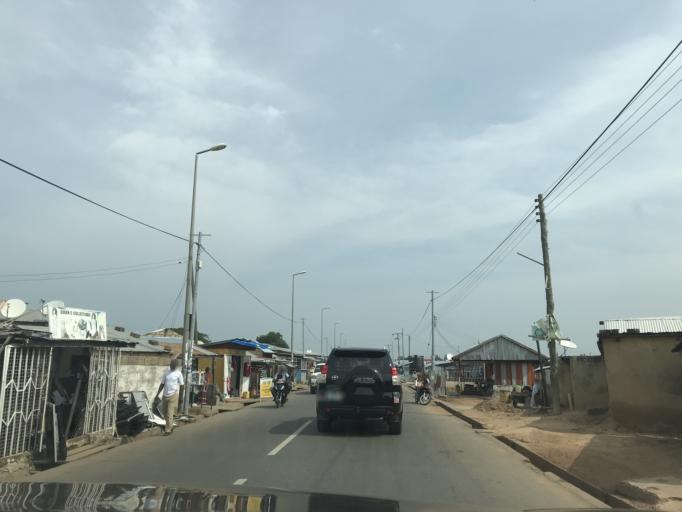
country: GH
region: Upper West
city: Wa
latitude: 10.0676
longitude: -2.5016
